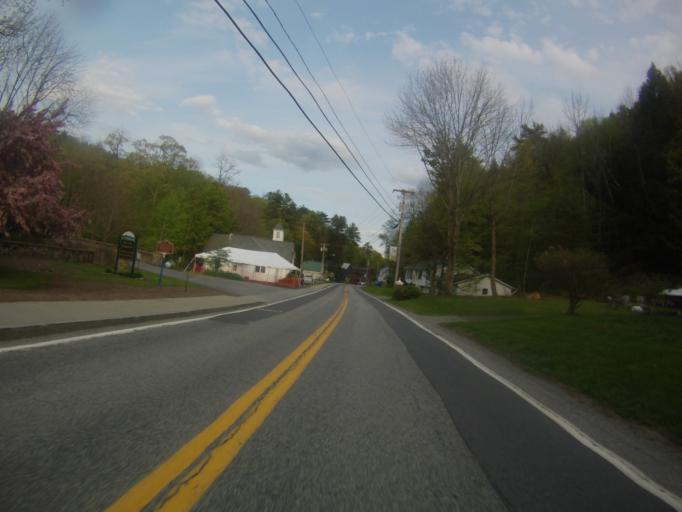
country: US
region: New York
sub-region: Essex County
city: Ticonderoga
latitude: 43.7486
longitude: -73.5028
